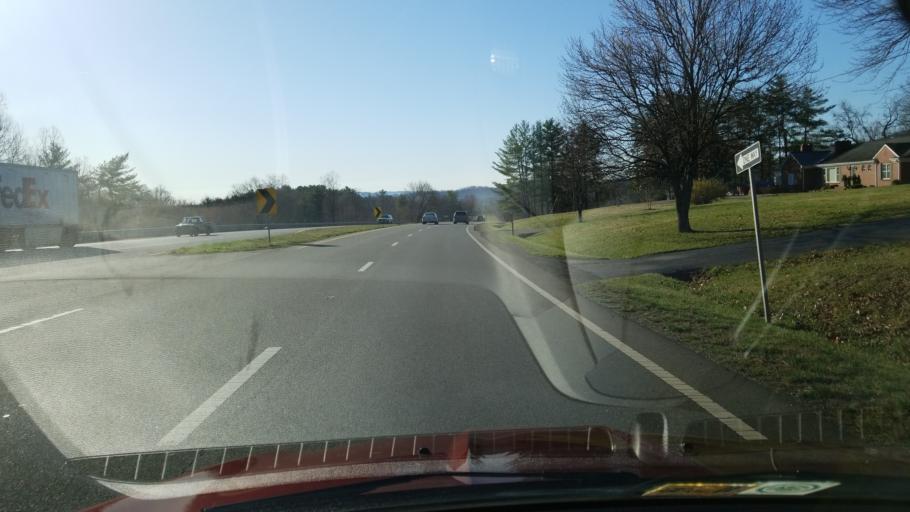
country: US
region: Virginia
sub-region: Franklin County
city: Rocky Mount
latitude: 37.0646
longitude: -79.8862
